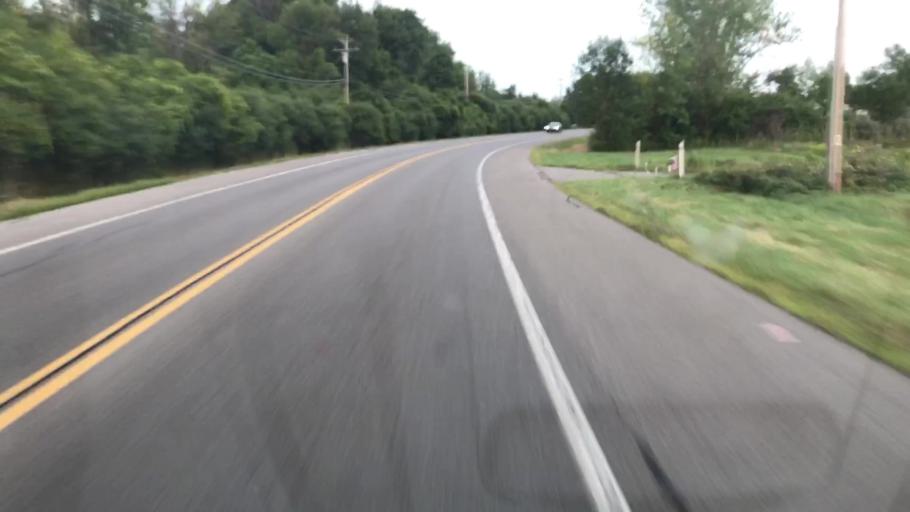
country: US
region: New York
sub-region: Onondaga County
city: North Syracuse
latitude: 43.1418
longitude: -76.1798
